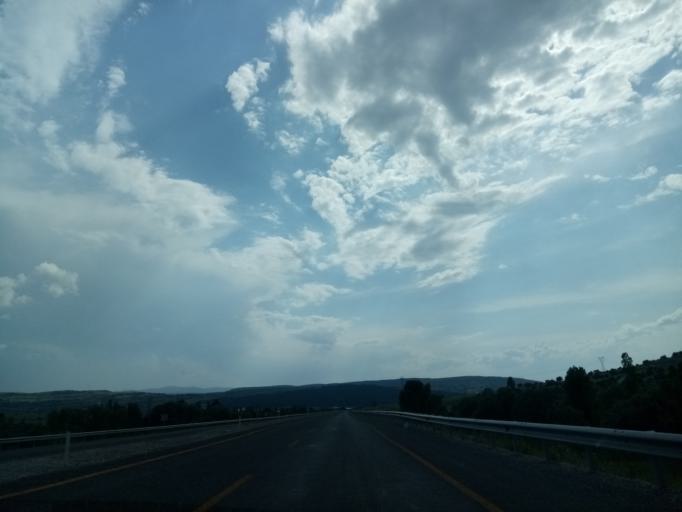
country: TR
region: Isparta
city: Bagkonak
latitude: 38.2009
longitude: 31.2569
